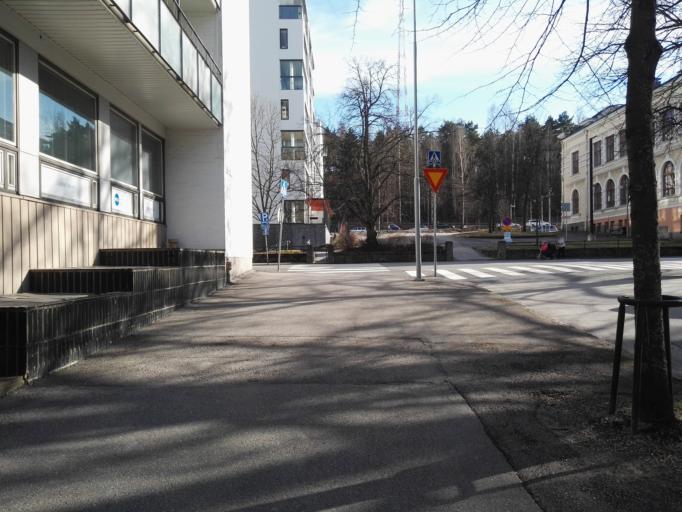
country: FI
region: Paijanne Tavastia
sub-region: Lahti
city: Lahti
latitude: 60.9820
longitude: 25.6505
